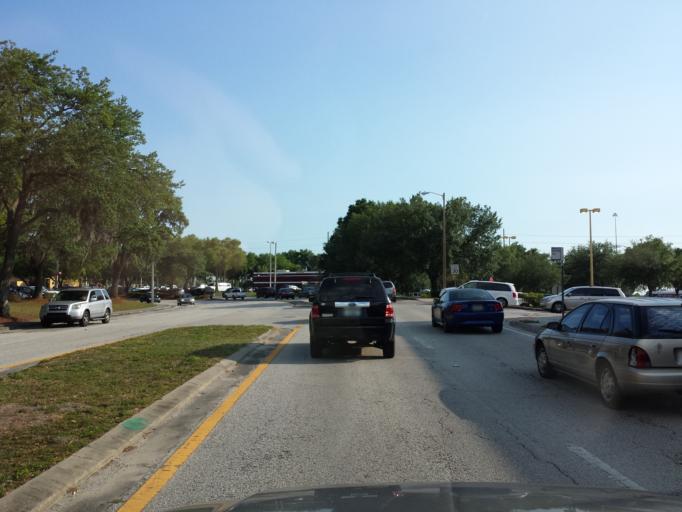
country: US
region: Florida
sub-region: Hillsborough County
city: Brandon
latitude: 27.9423
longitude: -82.3254
